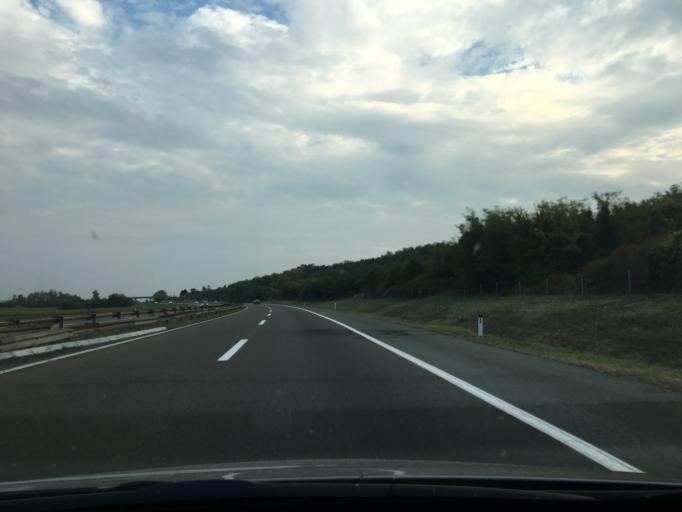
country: RS
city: Lugavcina
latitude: 44.4500
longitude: 21.0454
